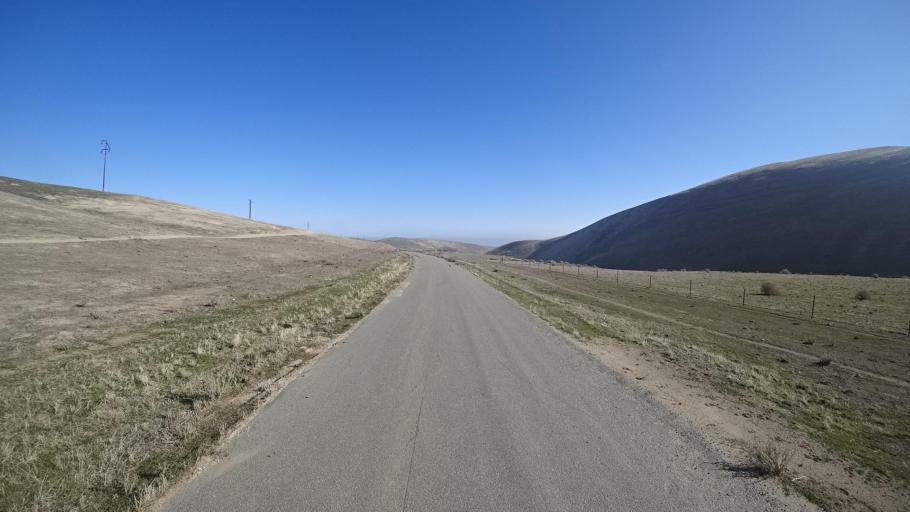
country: US
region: California
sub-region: Kern County
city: Taft Heights
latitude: 35.2293
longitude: -119.6665
